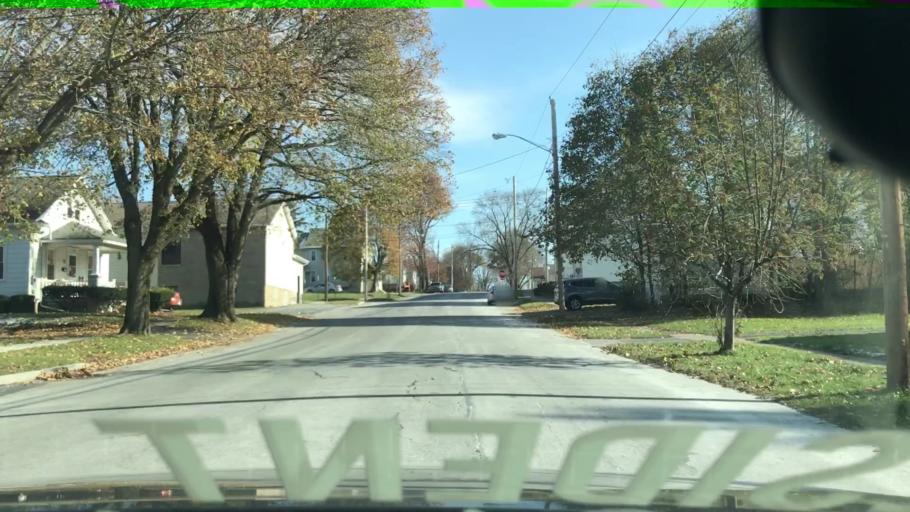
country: US
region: New York
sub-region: Cayuga County
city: Auburn
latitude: 42.9398
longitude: -76.5794
